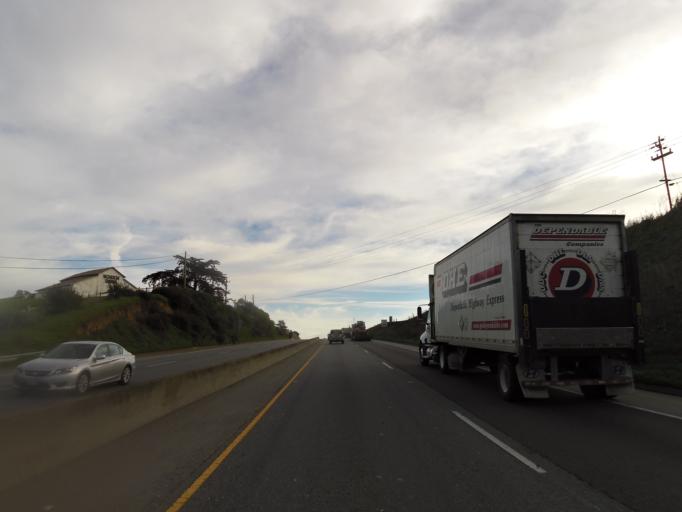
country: US
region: California
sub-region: Monterey County
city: Prunedale
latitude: 36.7543
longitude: -121.6645
